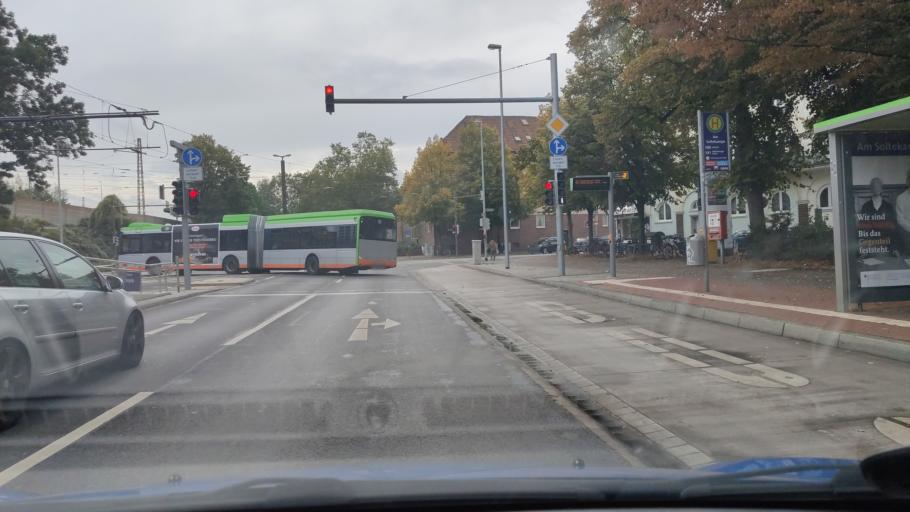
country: DE
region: Lower Saxony
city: Ronnenberg
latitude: 52.3575
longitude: 9.6769
